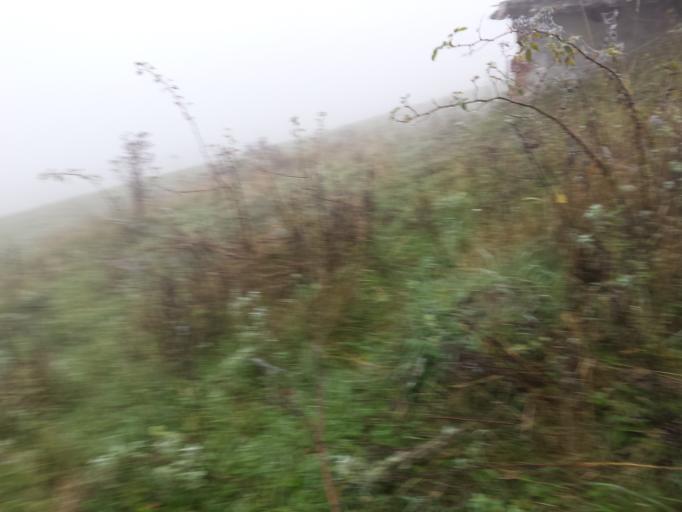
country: RO
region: Cluj
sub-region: Comuna Baciu
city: Baciu
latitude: 46.7739
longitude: 23.5470
